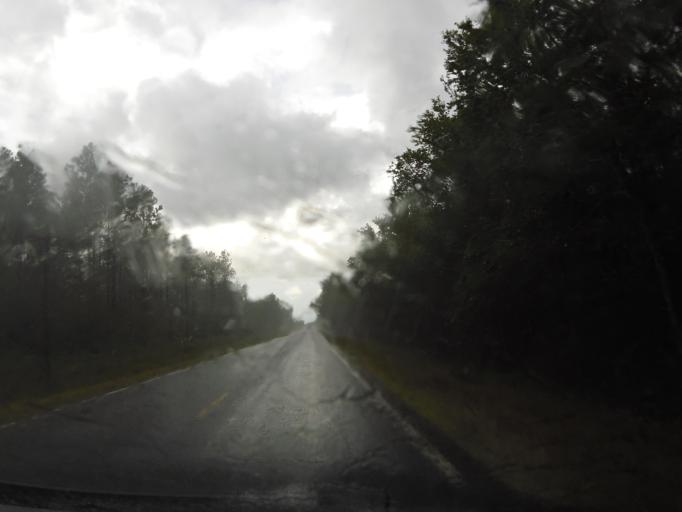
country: US
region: Florida
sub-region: Nassau County
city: Hilliard
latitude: 30.5410
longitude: -82.0400
